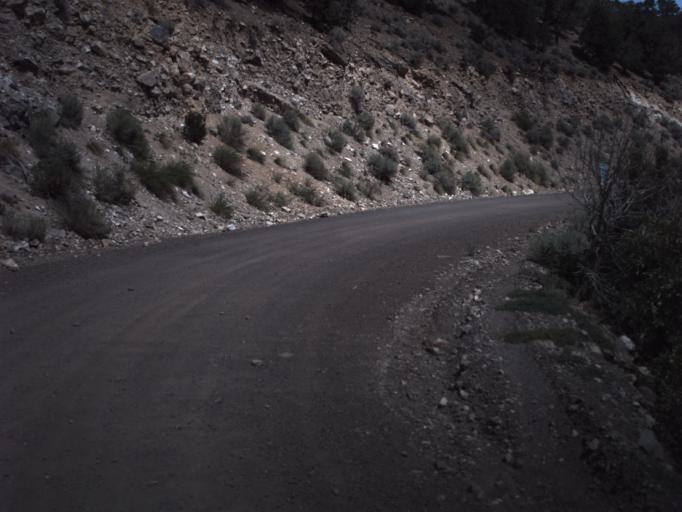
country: US
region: Utah
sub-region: Piute County
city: Junction
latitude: 38.2542
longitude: -112.3088
